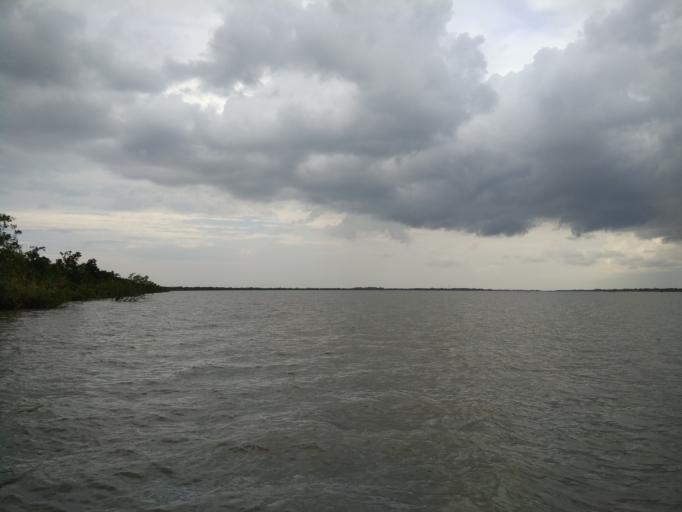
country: IN
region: West Bengal
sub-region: North 24 Parganas
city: Gosaba
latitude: 22.2184
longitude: 89.2413
